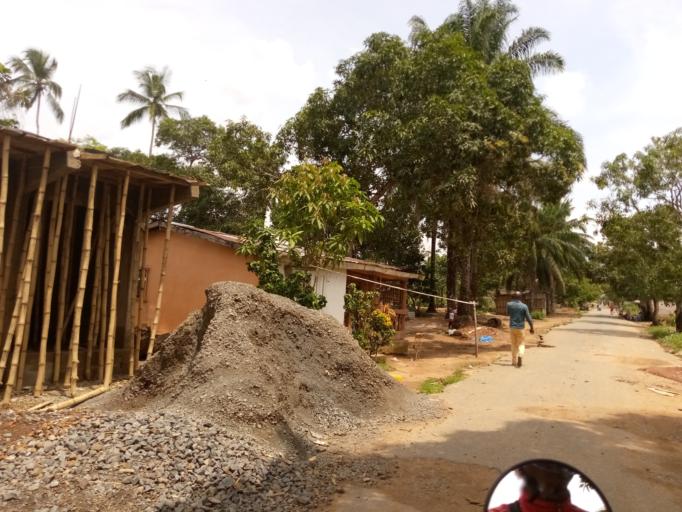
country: SL
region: Western Area
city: Waterloo
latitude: 8.3342
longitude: -13.0180
